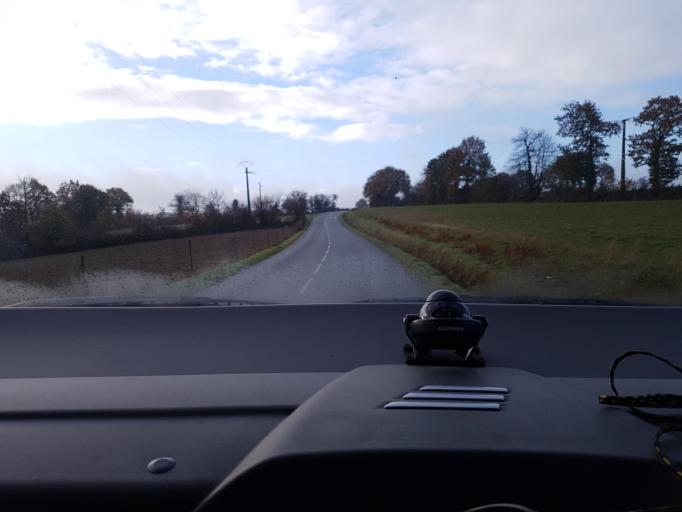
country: FR
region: Brittany
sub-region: Departement d'Ille-et-Vilaine
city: La Bouexiere
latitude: 48.1871
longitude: -1.4248
